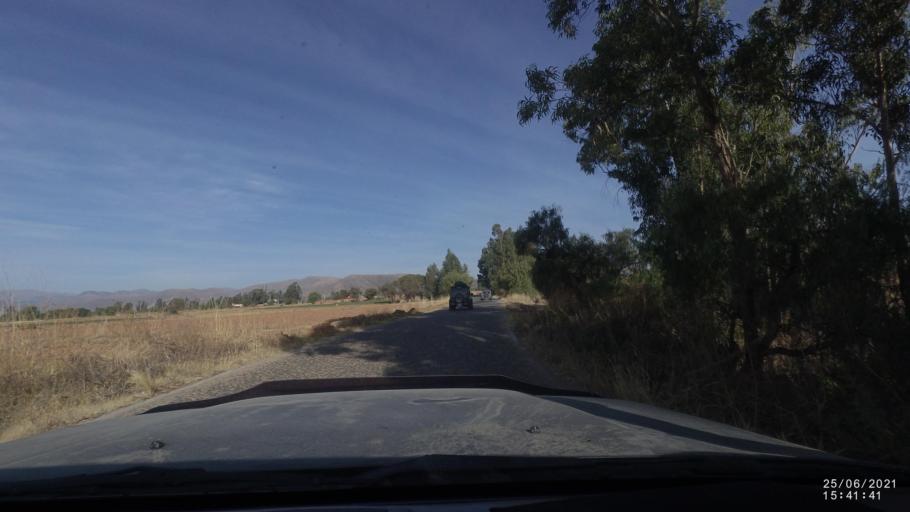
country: BO
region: Cochabamba
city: Cliza
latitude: -17.6352
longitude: -65.9168
